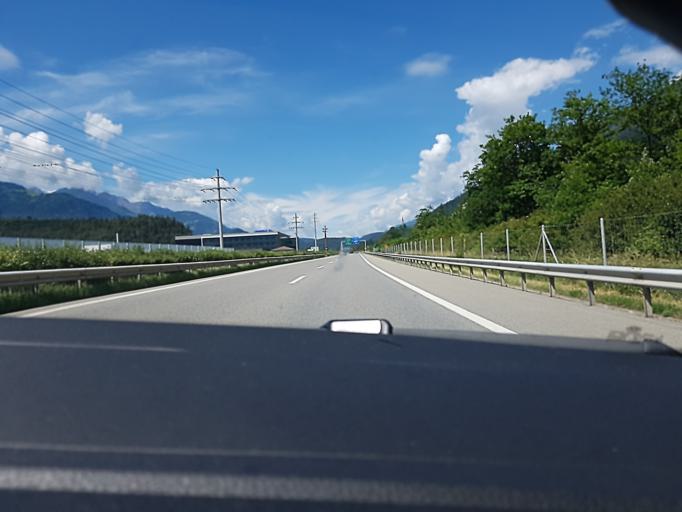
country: CH
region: Grisons
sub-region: Imboden District
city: Domat
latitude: 46.8326
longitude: 9.4316
